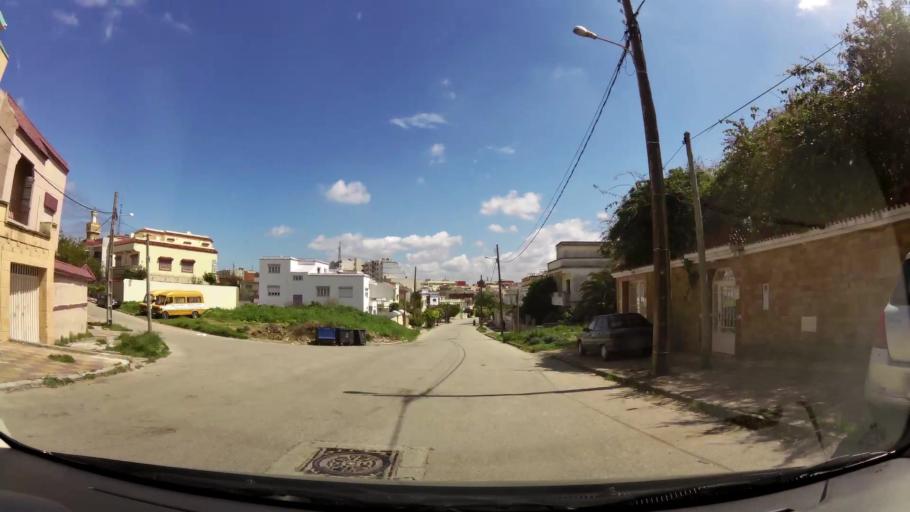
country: MA
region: Tanger-Tetouan
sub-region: Tanger-Assilah
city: Tangier
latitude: 35.7700
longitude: -5.8342
